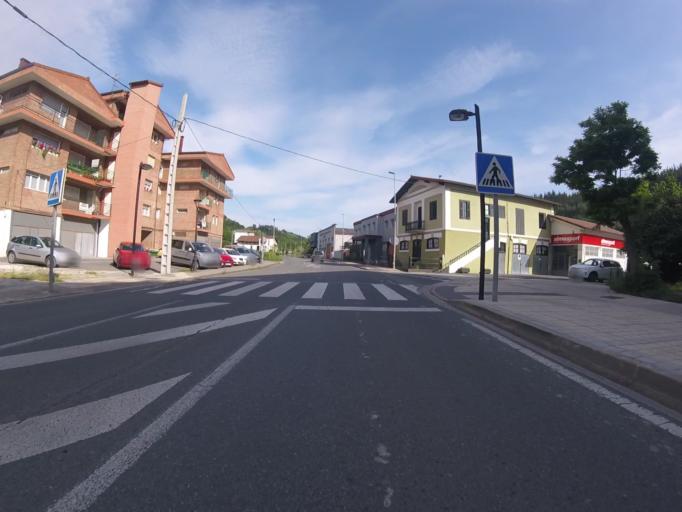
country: ES
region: Basque Country
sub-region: Provincia de Guipuzcoa
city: Ormaiztegui
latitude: 43.0438
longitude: -2.2566
